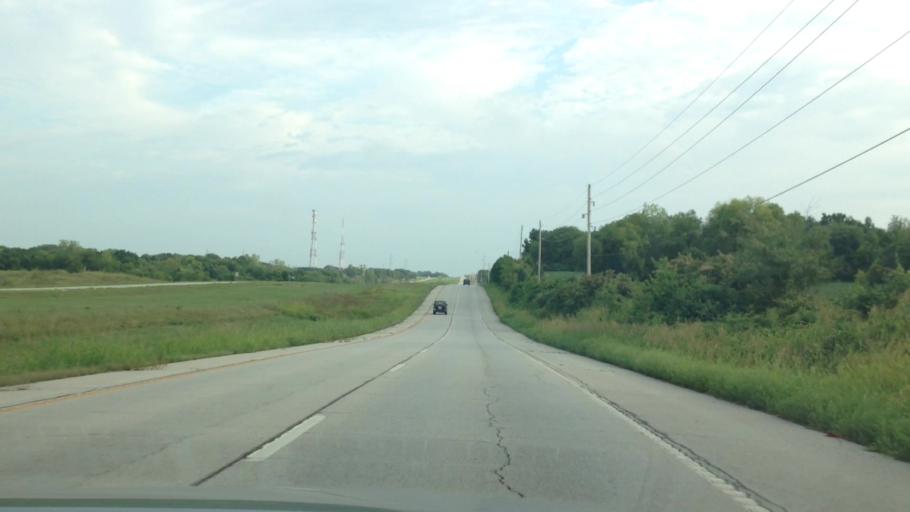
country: US
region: Missouri
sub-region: Clay County
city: Smithville
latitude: 39.3439
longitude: -94.5842
